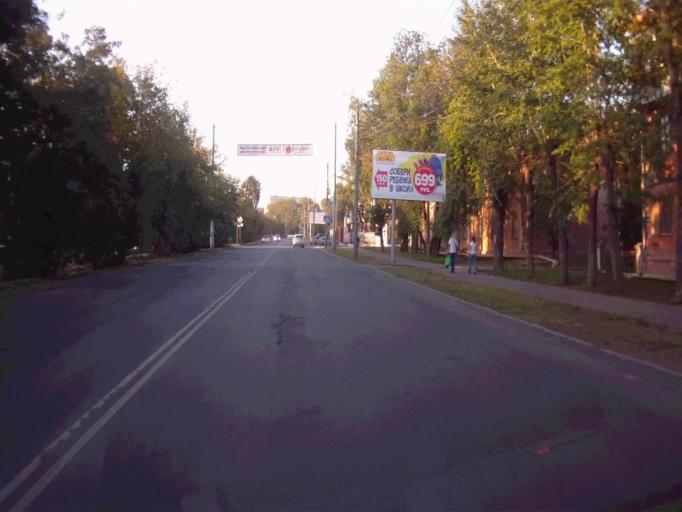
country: RU
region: Chelyabinsk
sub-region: Gorod Chelyabinsk
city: Chelyabinsk
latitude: 55.1650
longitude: 61.4344
